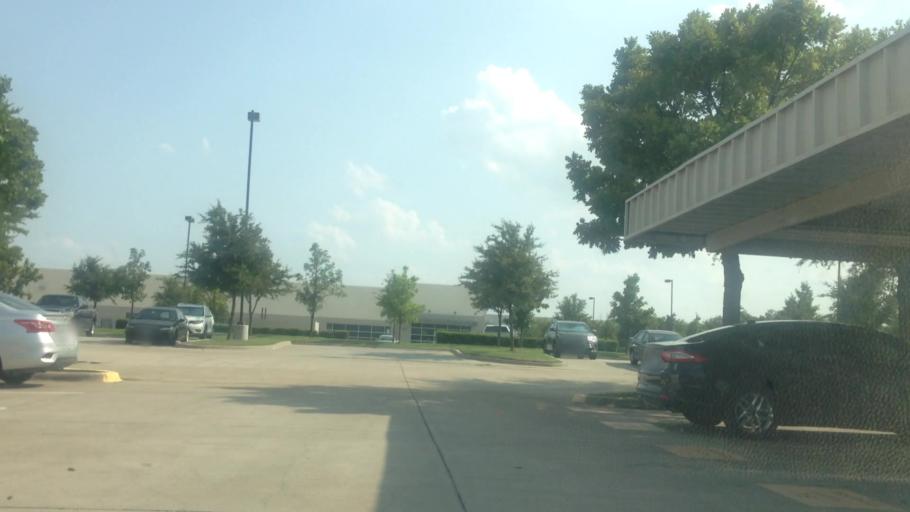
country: US
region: Texas
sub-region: Dallas County
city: Coppell
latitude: 32.9372
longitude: -96.9960
